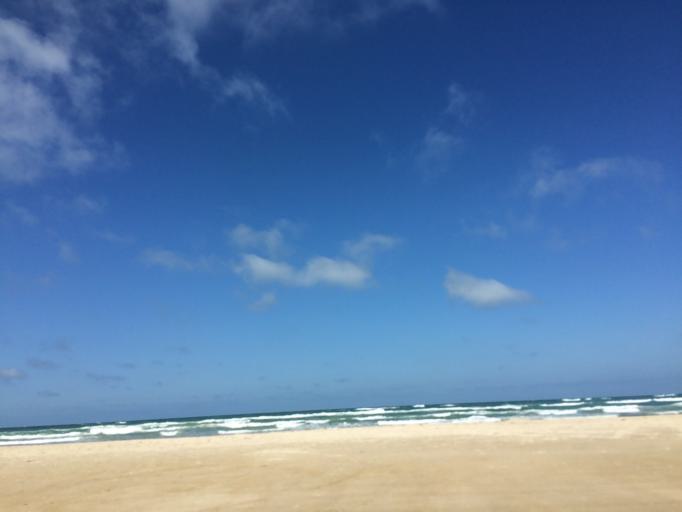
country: DK
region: North Denmark
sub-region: Jammerbugt Kommune
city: Brovst
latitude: 57.2231
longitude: 9.5358
